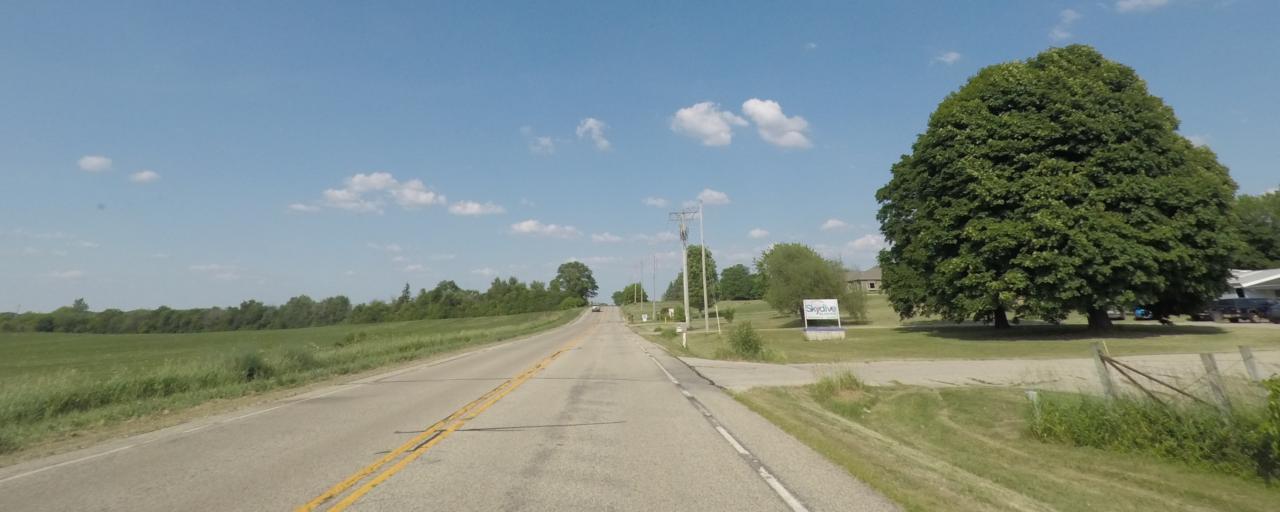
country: US
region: Wisconsin
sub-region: Walworth County
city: Potter Lake
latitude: 42.8024
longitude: -88.3720
